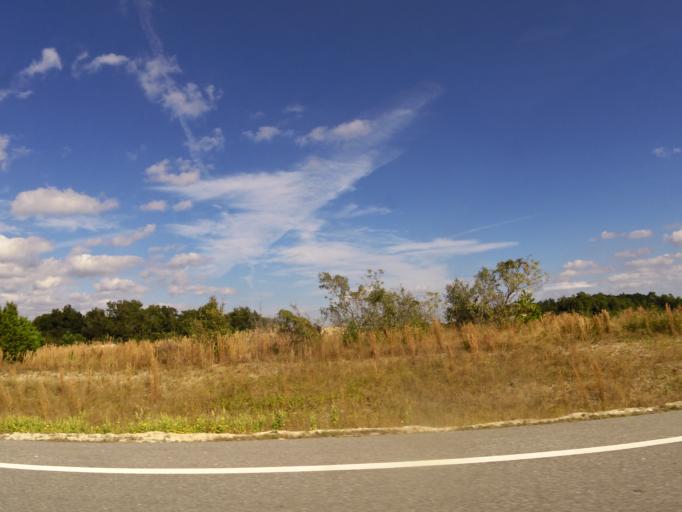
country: US
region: Florida
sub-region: Duval County
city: Jacksonville
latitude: 30.4130
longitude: -81.6256
